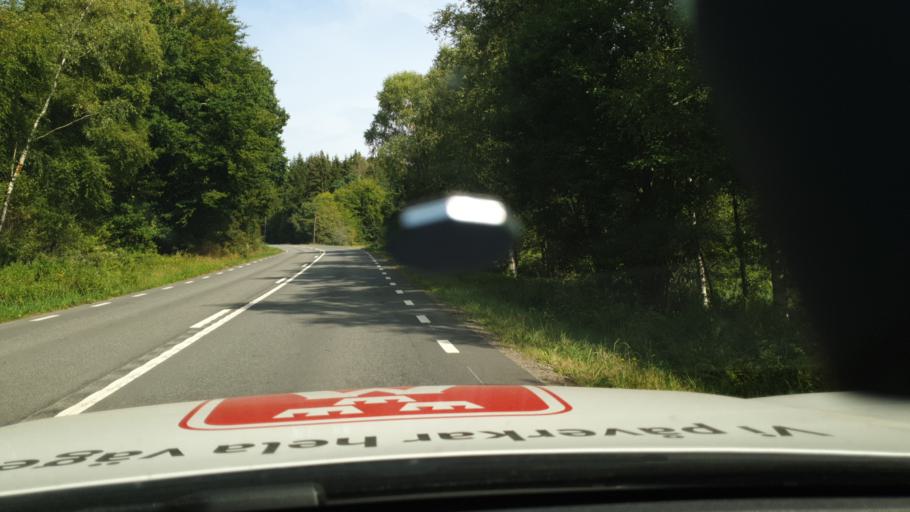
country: SE
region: Skane
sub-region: Simrishamns Kommun
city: Kivik
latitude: 55.6054
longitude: 14.1413
